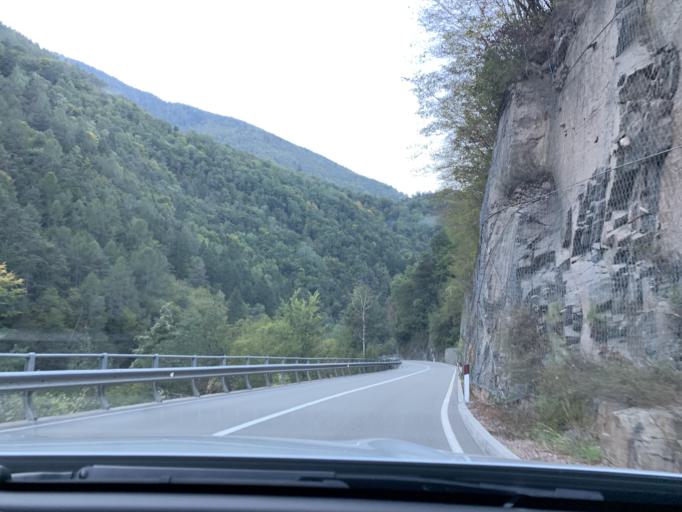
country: IT
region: Trentino-Alto Adige
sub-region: Bolzano
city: Cornedo All'Isarco
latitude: 46.4649
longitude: 11.4119
